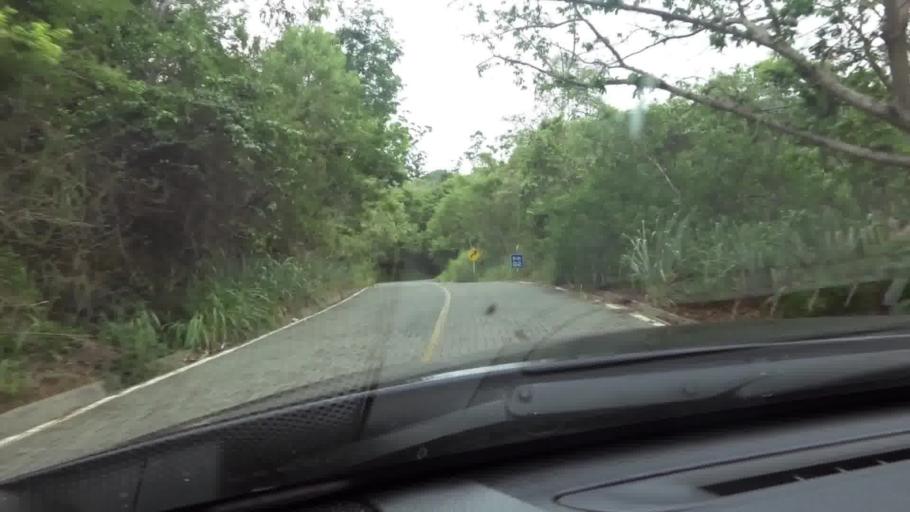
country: BR
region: Espirito Santo
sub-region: Guarapari
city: Guarapari
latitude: -20.6150
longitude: -40.5326
